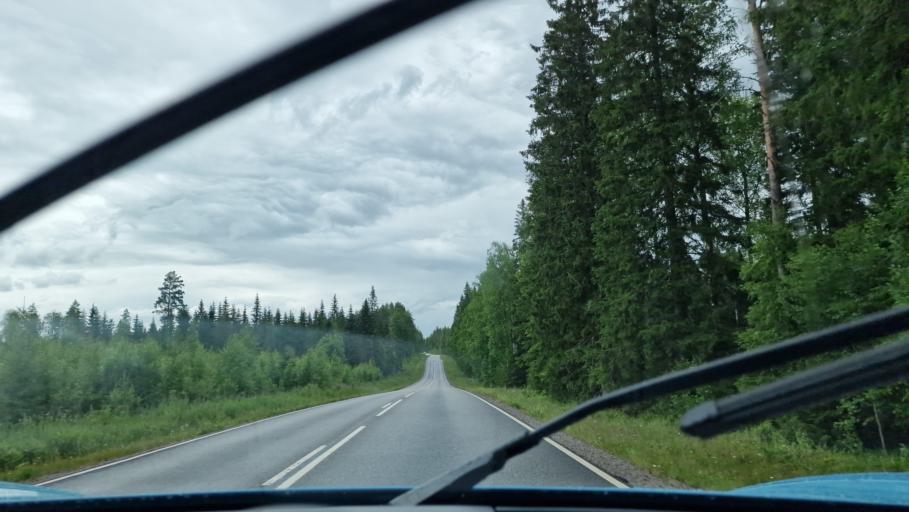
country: FI
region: Central Finland
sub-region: Saarijaervi-Viitasaari
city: Pylkoenmaeki
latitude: 62.6081
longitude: 24.5847
